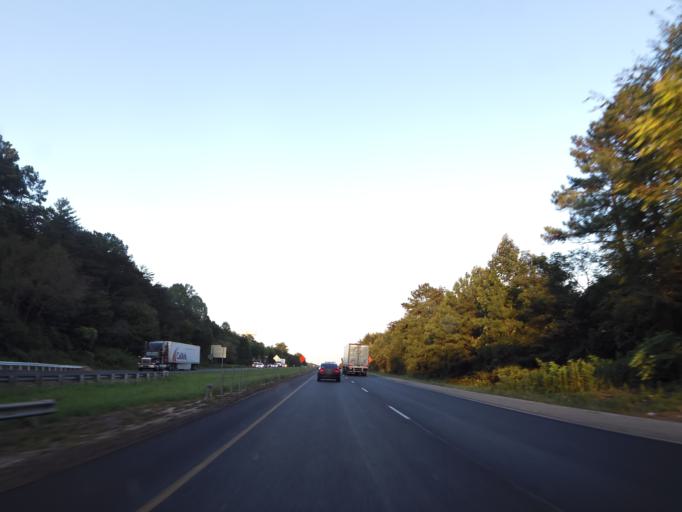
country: US
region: Tennessee
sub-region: Roane County
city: Kingston
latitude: 35.8721
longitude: -84.4843
